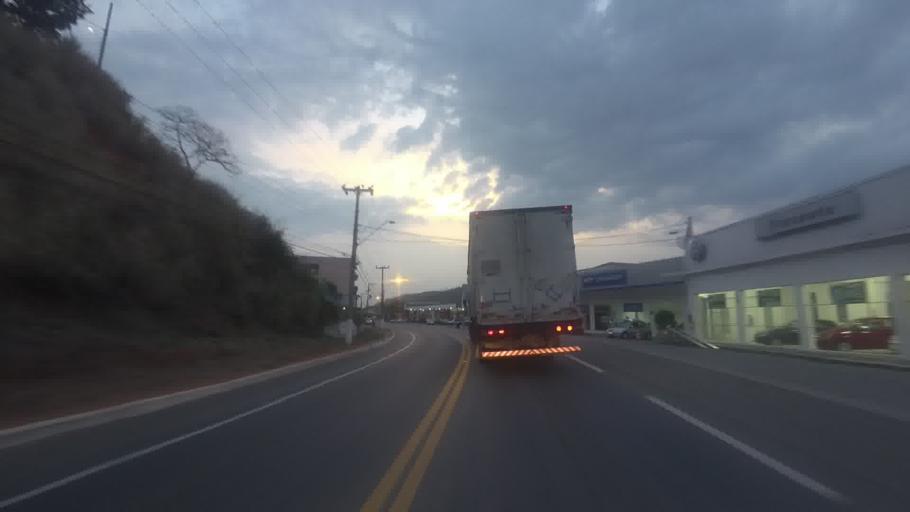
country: BR
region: Minas Gerais
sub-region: Alem Paraiba
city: Alem Paraiba
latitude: -21.8892
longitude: -42.7028
